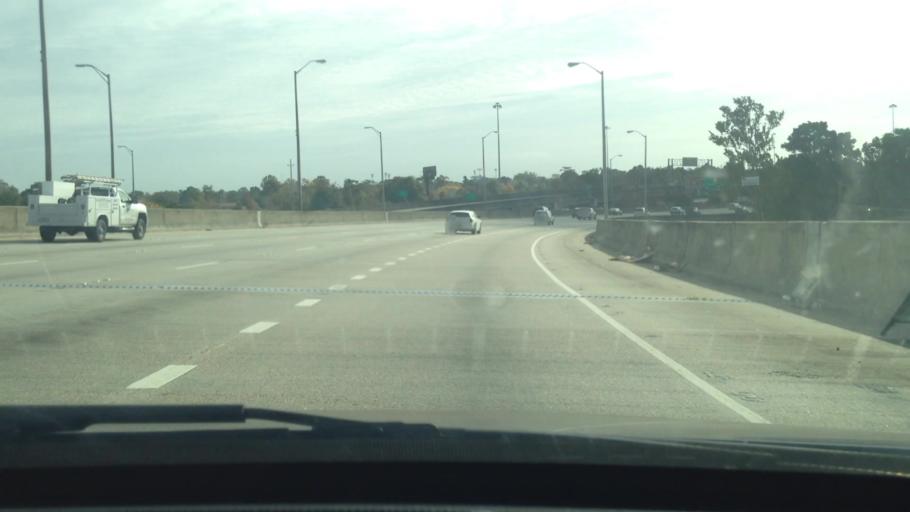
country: US
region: Louisiana
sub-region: Jefferson Parish
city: Gretna
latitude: 29.9374
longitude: -90.0408
